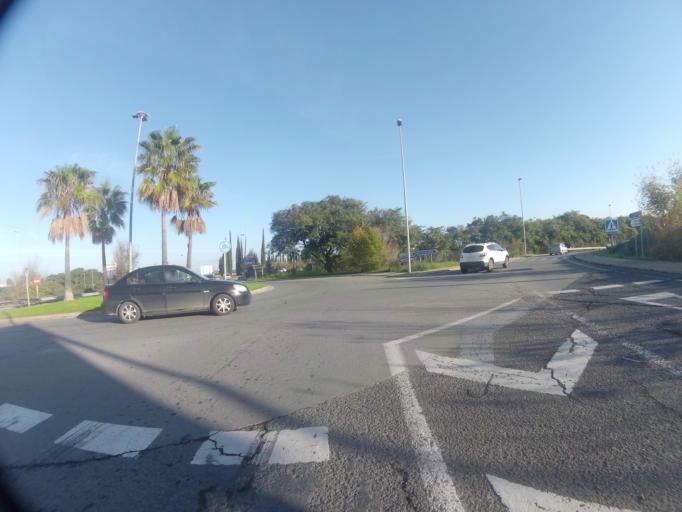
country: ES
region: Andalusia
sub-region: Provincia de Huelva
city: Huelva
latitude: 37.2831
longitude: -6.9351
